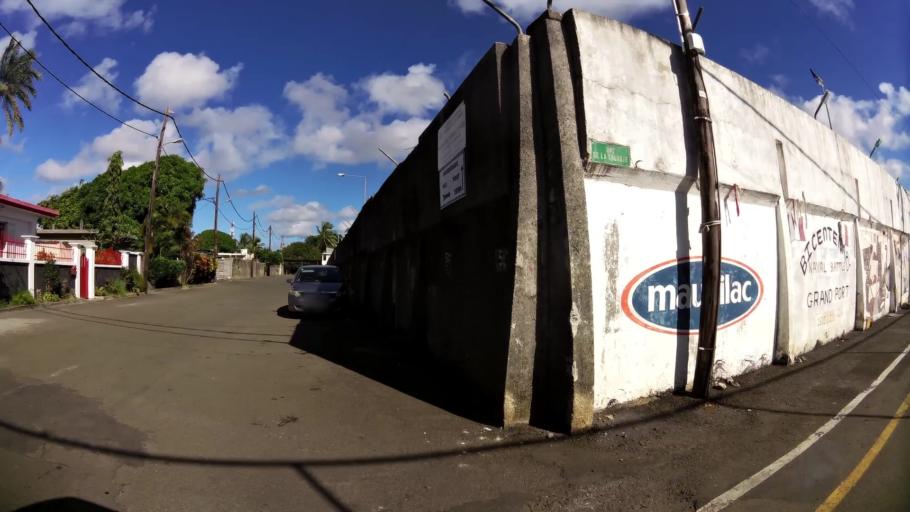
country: MU
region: Grand Port
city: Mahebourg
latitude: -20.4046
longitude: 57.7063
